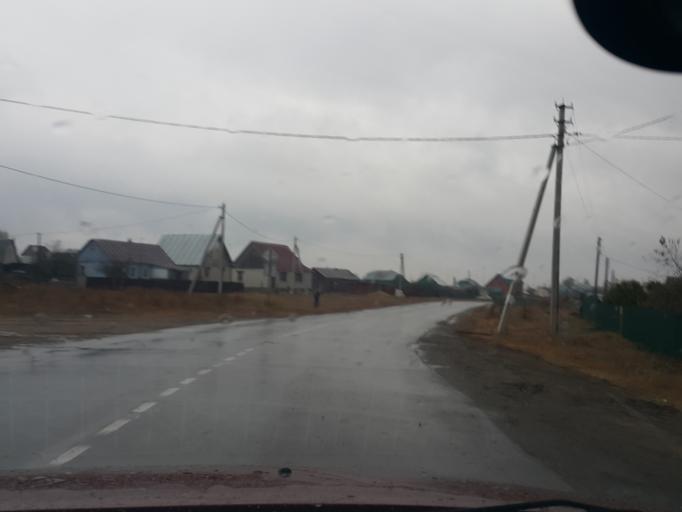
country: RU
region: Tambov
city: Kotovsk
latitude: 52.5319
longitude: 41.4762
